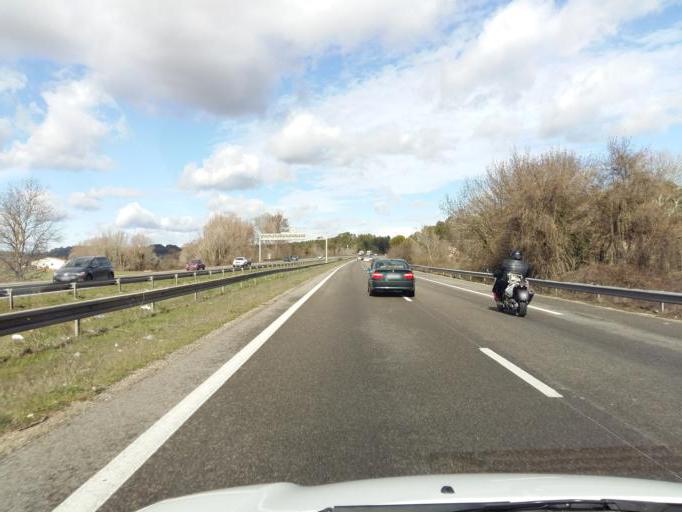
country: FR
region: Provence-Alpes-Cote d'Azur
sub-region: Departement des Bouches-du-Rhone
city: Bouc-Bel-Air
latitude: 43.4952
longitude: 5.4069
